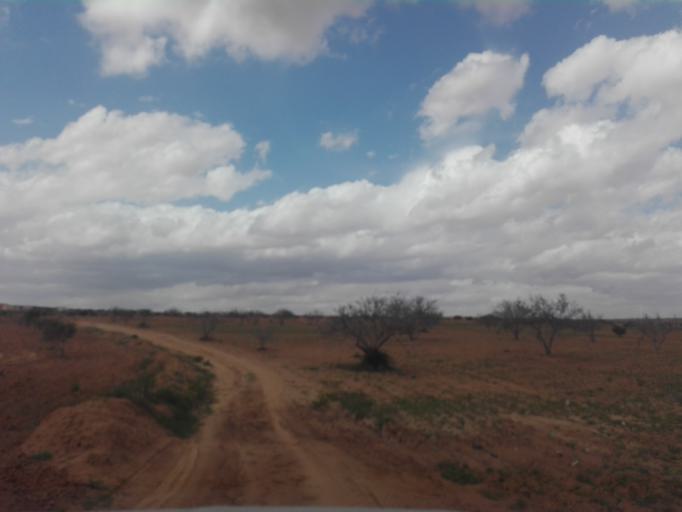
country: TN
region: Safaqis
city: Sfax
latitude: 34.6993
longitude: 10.4426
